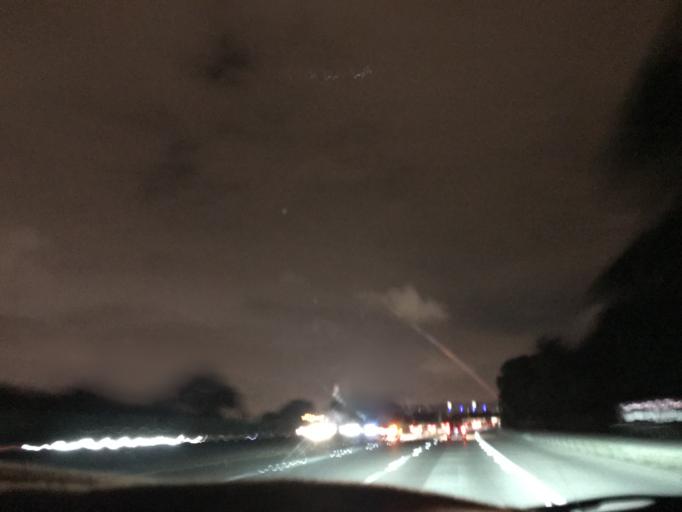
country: TW
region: Taiwan
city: Daxi
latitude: 24.8554
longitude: 121.2069
